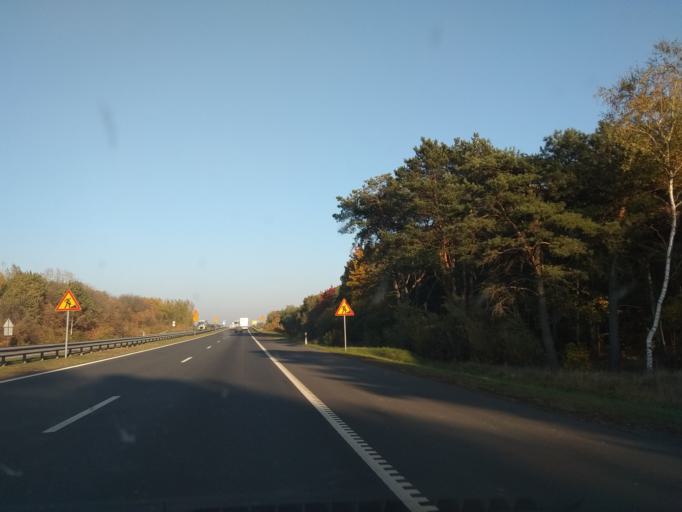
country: BY
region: Brest
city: Zhabinka
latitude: 52.1333
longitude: 23.9371
